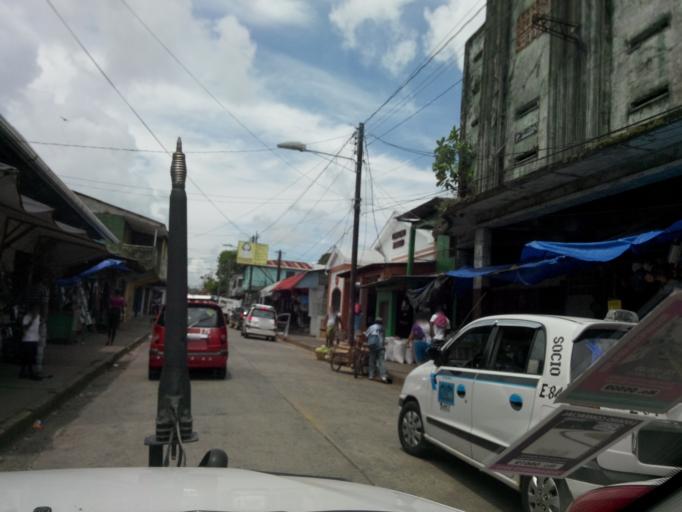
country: NI
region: Atlantico Sur
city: Bluefields
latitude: 12.0120
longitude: -83.7624
